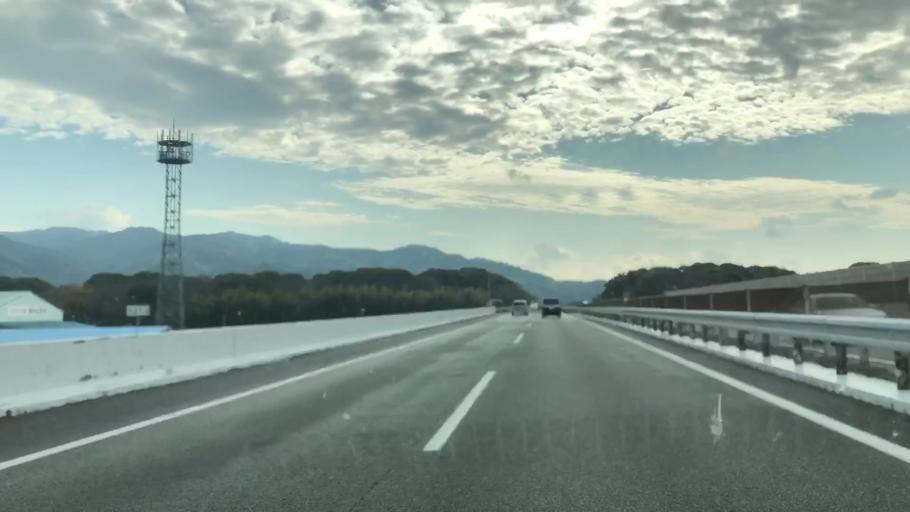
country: JP
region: Fukuoka
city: Setakamachi-takayanagi
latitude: 33.1850
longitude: 130.5188
